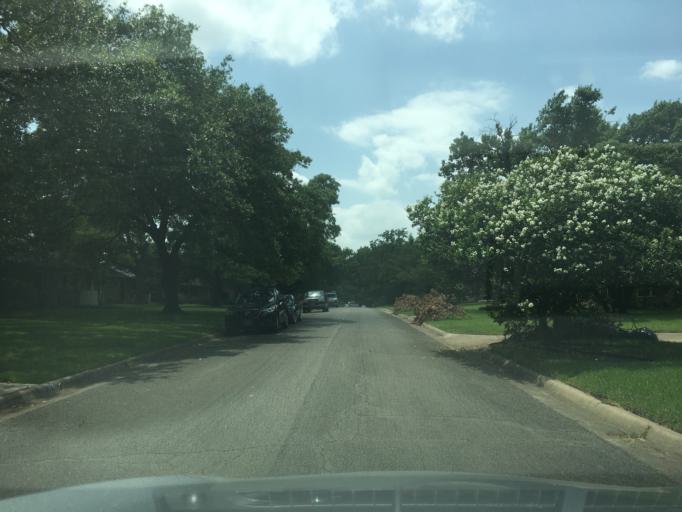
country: US
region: Texas
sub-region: Dallas County
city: Addison
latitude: 32.9054
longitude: -96.8243
